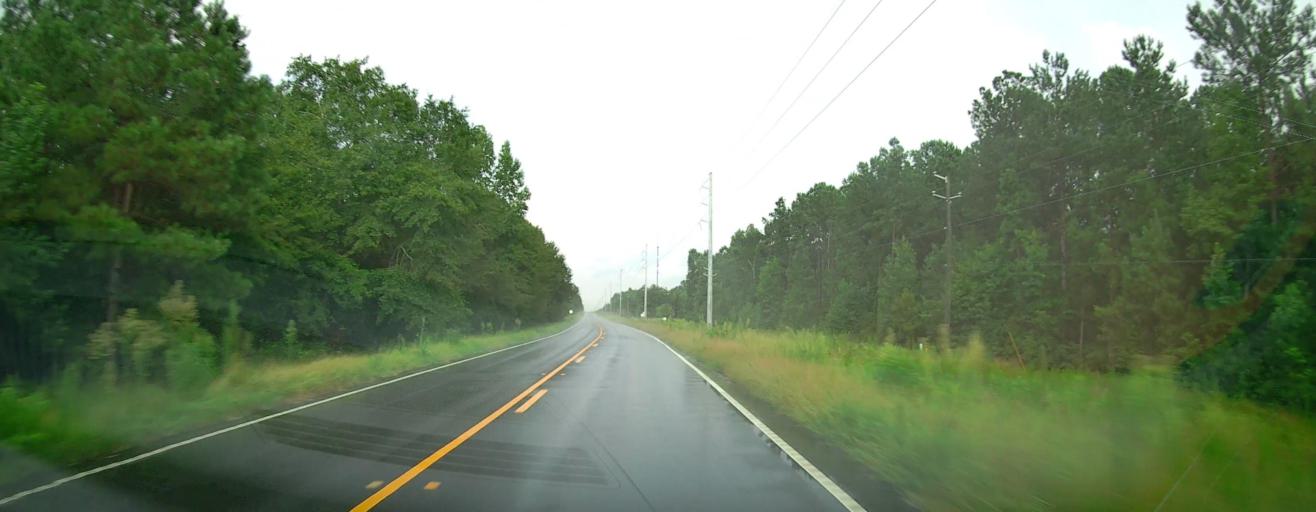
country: US
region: Georgia
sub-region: Dodge County
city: Chester
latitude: 32.5738
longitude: -83.1990
